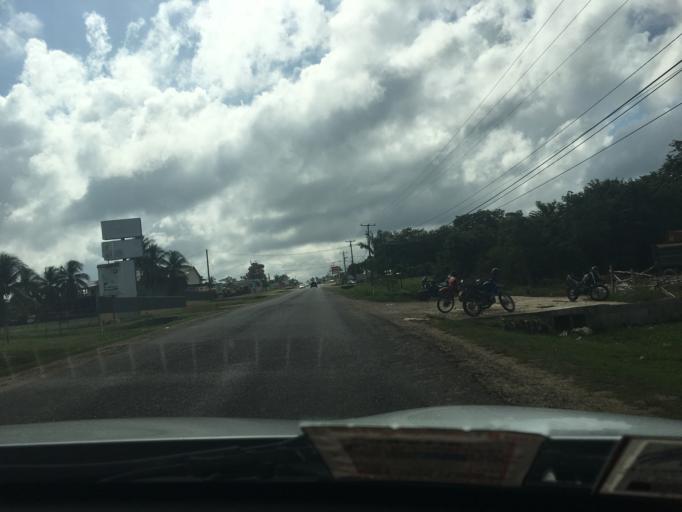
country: BZ
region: Cayo
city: Belmopan
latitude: 17.2482
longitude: -88.7842
